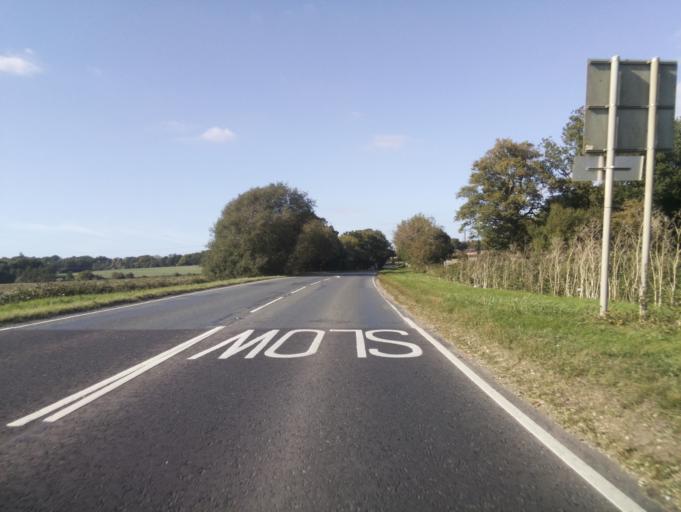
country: GB
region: England
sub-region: Hampshire
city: Tadley
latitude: 51.3178
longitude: -1.1205
